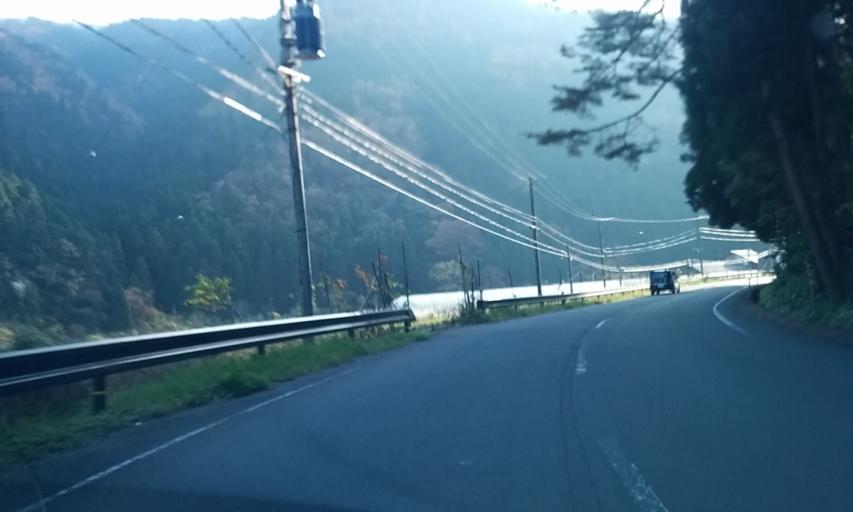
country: JP
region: Fukui
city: Obama
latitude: 35.2972
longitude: 135.6155
